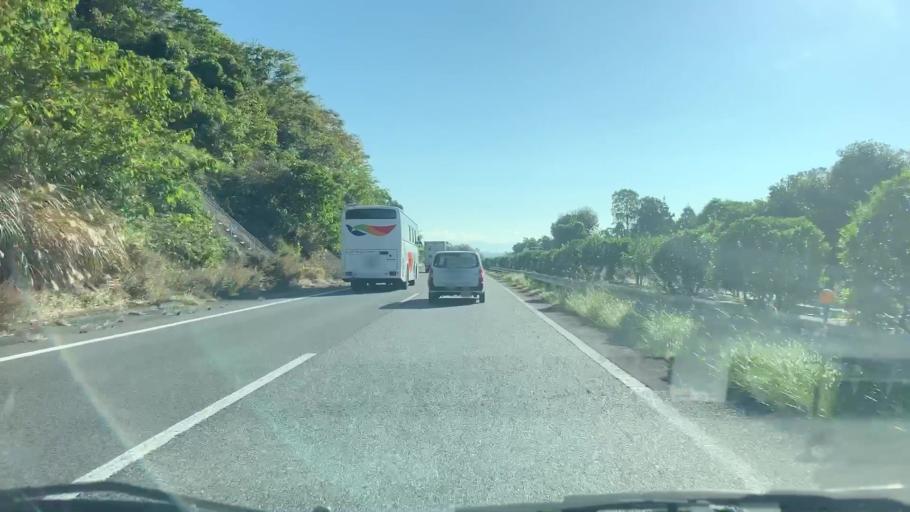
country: JP
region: Saga Prefecture
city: Saga-shi
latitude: 33.3084
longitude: 130.2250
